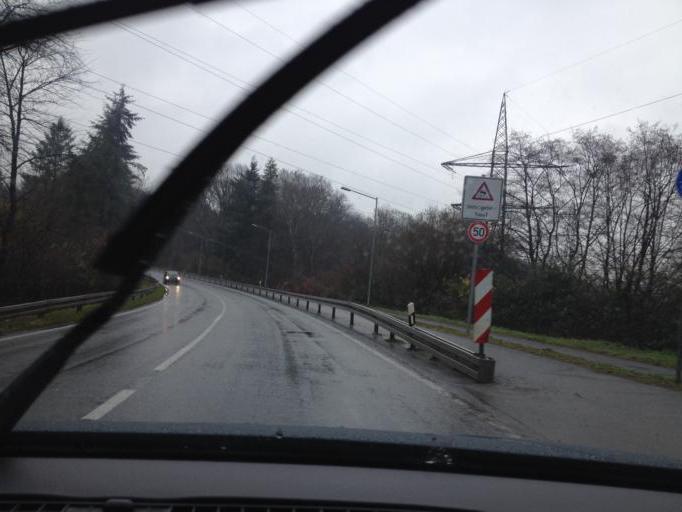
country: DE
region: Saarland
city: Neunkirchen
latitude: 49.3333
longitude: 7.1945
